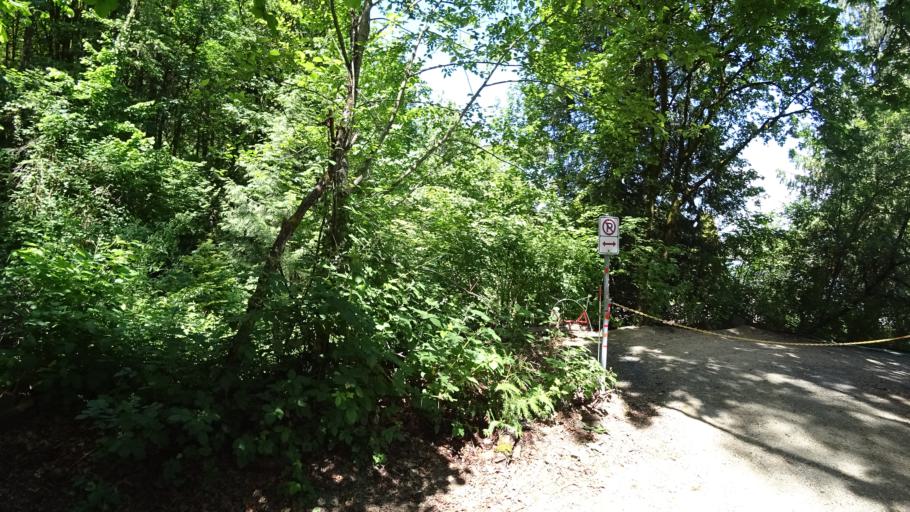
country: US
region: Oregon
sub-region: Washington County
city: Cedar Mill
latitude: 45.5914
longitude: -122.7817
